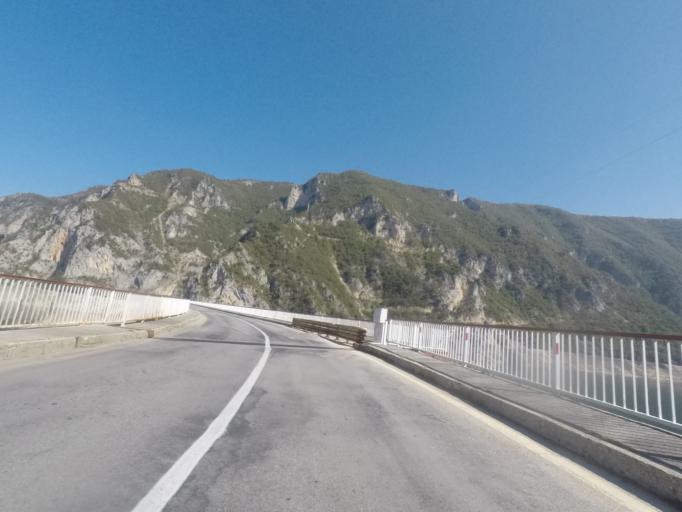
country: ME
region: Opstina Pluzine
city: Pluzine
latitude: 43.1650
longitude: 18.8561
